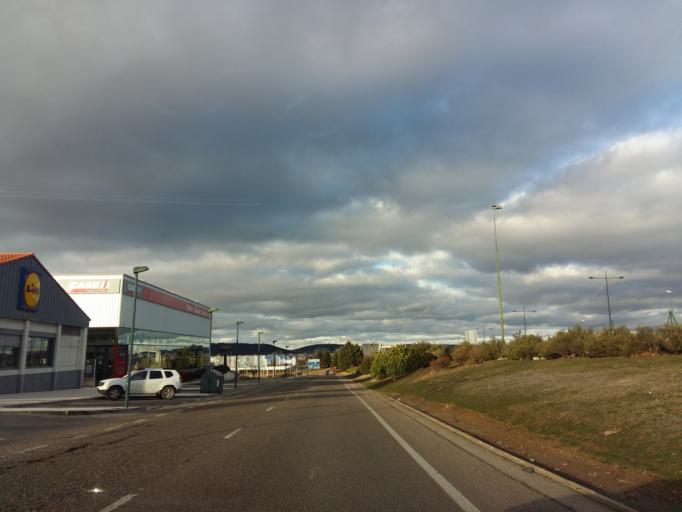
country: ES
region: Castille and Leon
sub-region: Provincia de Burgos
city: Villagonzalo-Pedernales
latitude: 42.3200
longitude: -3.7019
